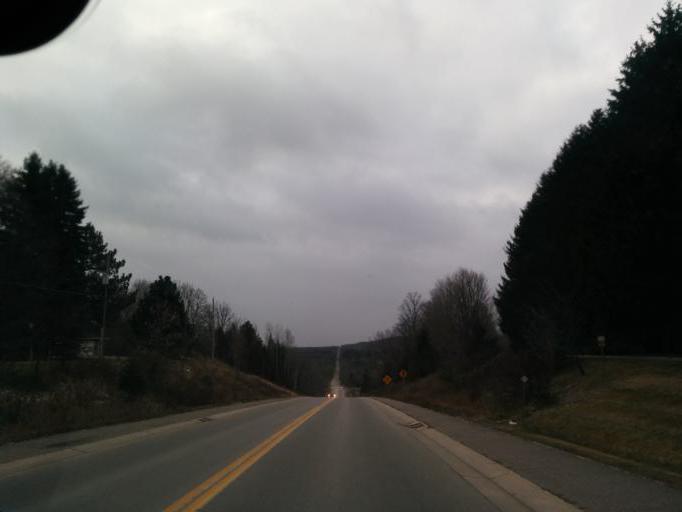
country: CA
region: Ontario
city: Brampton
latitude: 43.7955
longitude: -79.9214
